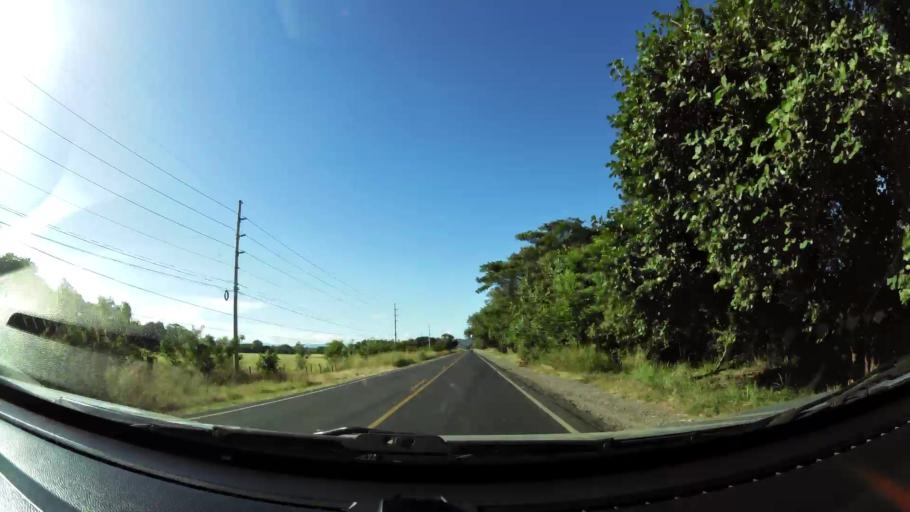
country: CR
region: Guanacaste
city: Belen
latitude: 10.4299
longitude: -85.5687
